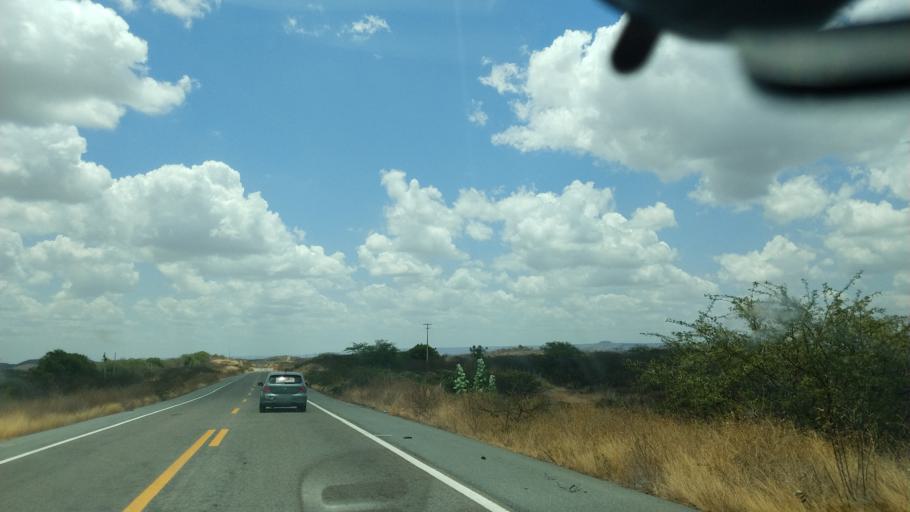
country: BR
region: Rio Grande do Norte
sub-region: Cerro Cora
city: Cerro Cora
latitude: -6.2096
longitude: -36.3082
